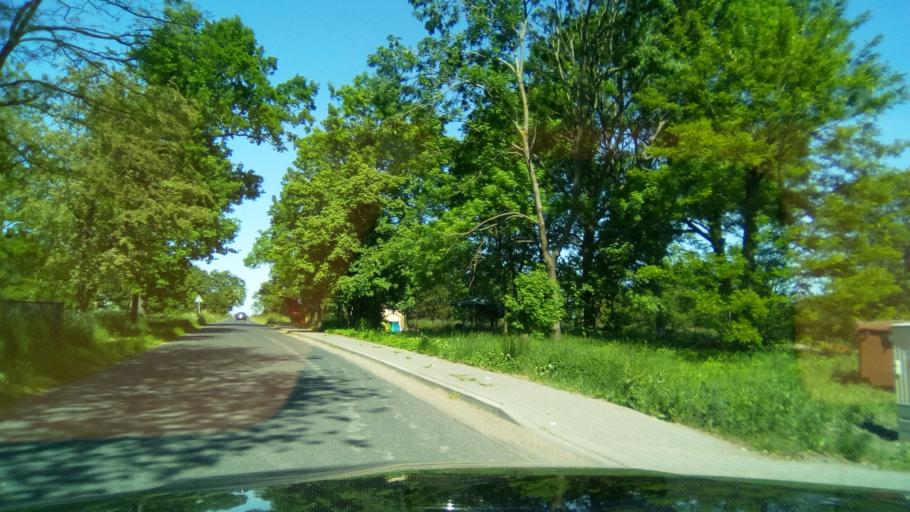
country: PL
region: Greater Poland Voivodeship
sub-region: Powiat gnieznienski
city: Niechanowo
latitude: 52.4555
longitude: 17.6199
